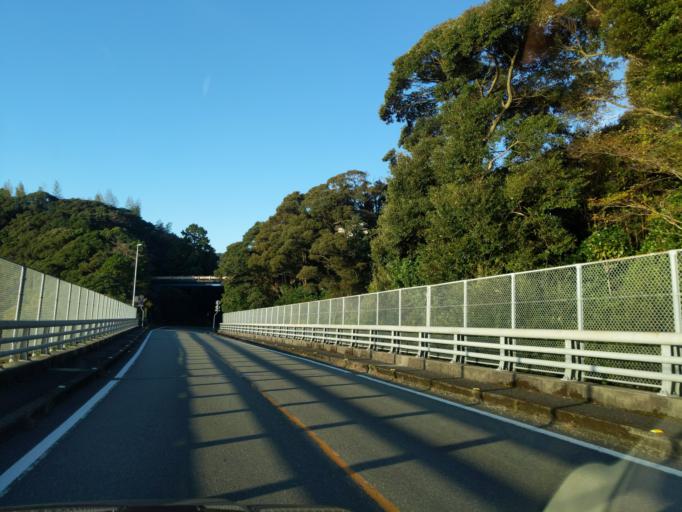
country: JP
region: Kochi
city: Muroto-misakicho
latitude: 33.5454
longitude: 134.2996
